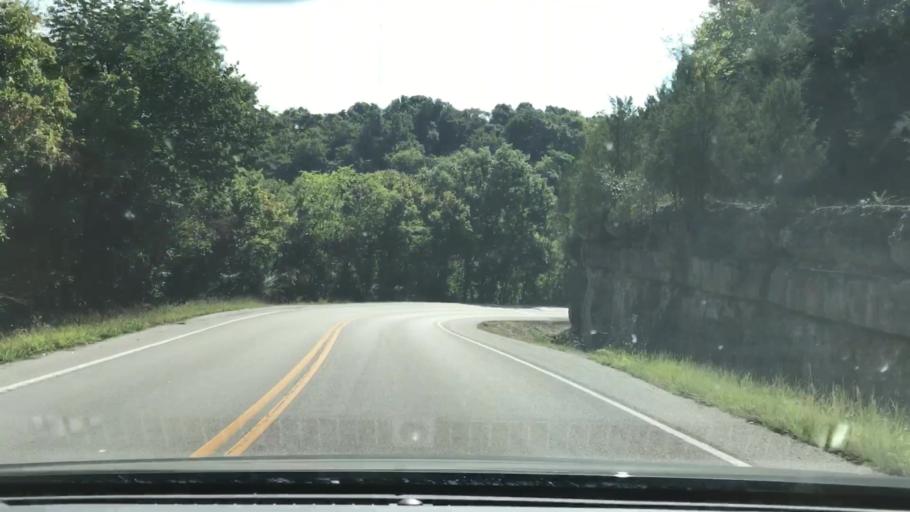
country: US
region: Tennessee
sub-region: Jackson County
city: Gainesboro
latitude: 36.3536
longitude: -85.6691
